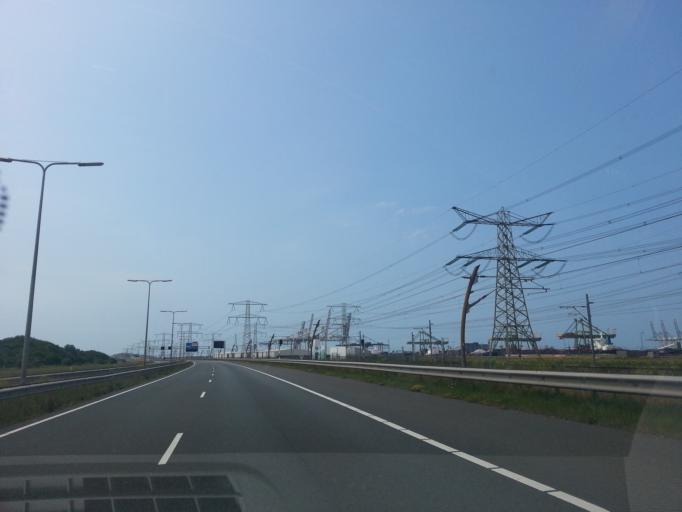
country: NL
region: South Holland
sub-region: Gemeente Rotterdam
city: Hoek van Holland
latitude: 51.9339
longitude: 4.0721
